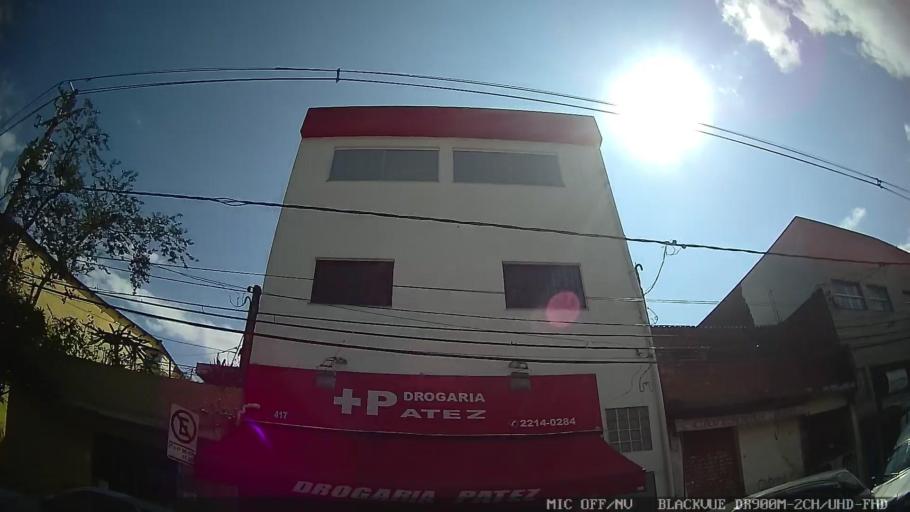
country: BR
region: Sao Paulo
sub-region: Guarulhos
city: Guarulhos
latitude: -23.4954
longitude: -46.4686
